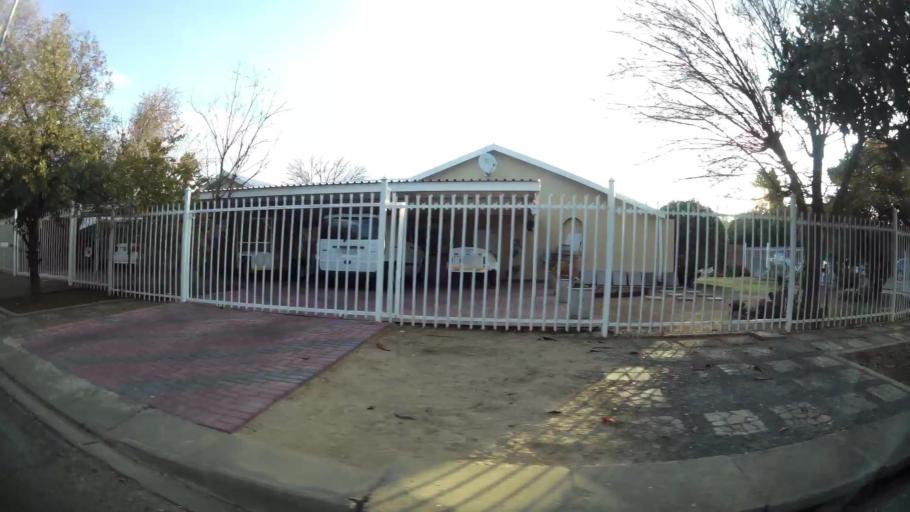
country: ZA
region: Orange Free State
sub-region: Mangaung Metropolitan Municipality
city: Bloemfontein
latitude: -29.1393
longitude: 26.1764
